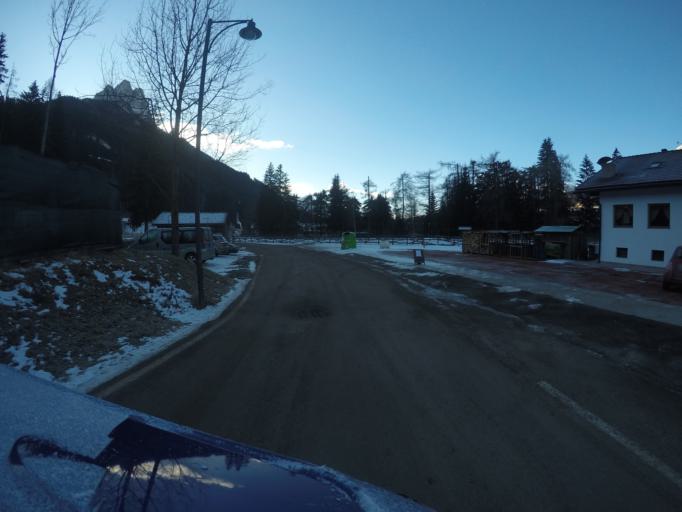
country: IT
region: Trentino-Alto Adige
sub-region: Provincia di Trento
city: Pozza di Fassa
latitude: 46.4274
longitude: 11.6871
